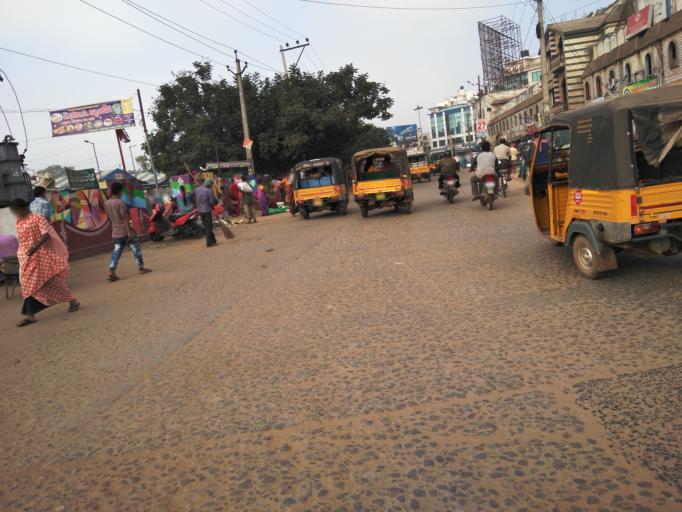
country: IN
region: Andhra Pradesh
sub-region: Nellore
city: Nellore
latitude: 14.4457
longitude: 79.9818
